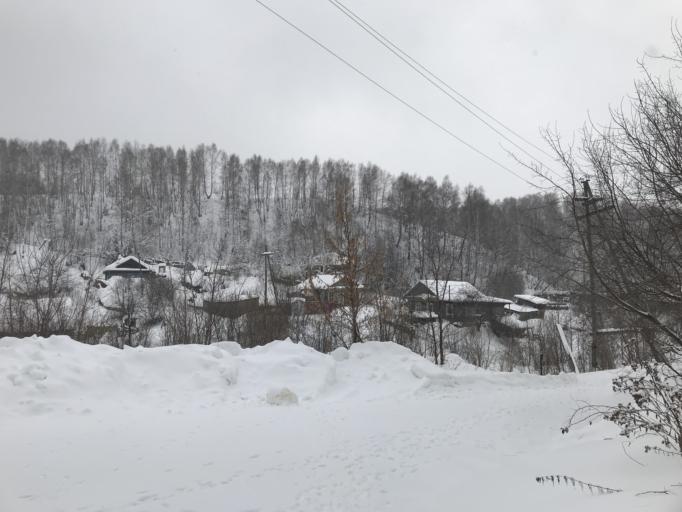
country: RU
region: Tjumen
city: Tobol'sk
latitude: 58.1984
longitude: 68.2596
